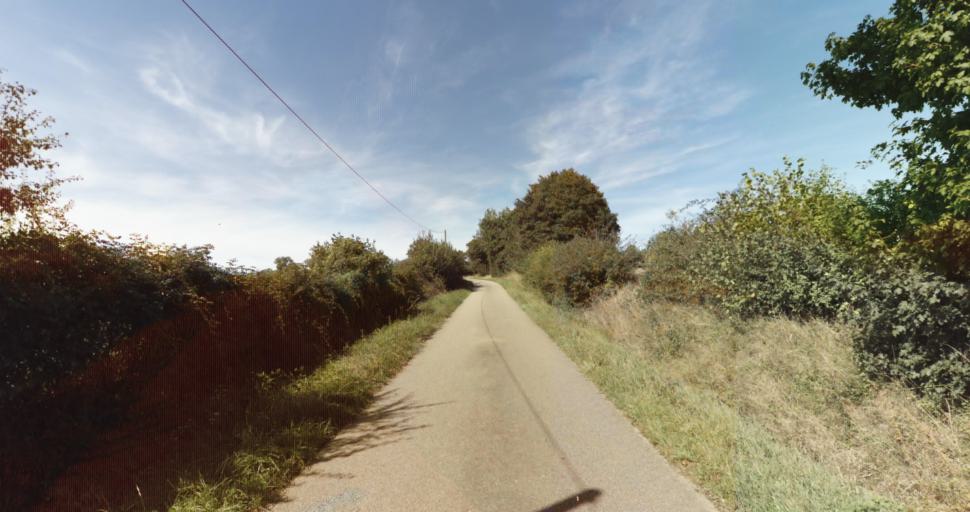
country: FR
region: Lower Normandy
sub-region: Departement de l'Orne
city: Gace
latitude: 48.7554
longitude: 0.2441
